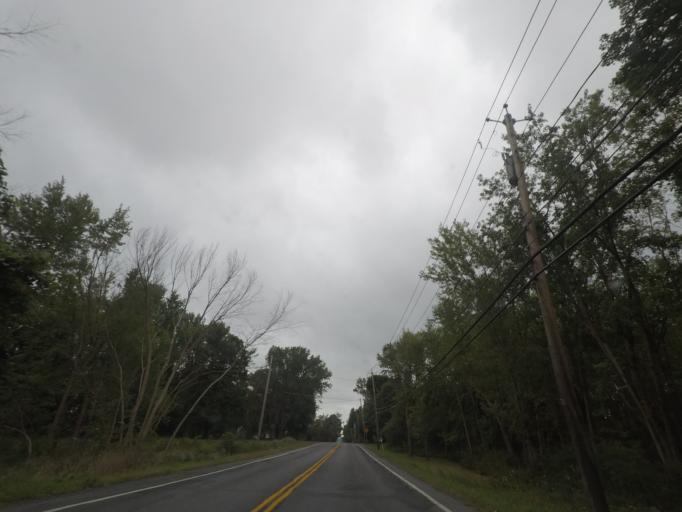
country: US
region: New York
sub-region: Rensselaer County
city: Hoosick Falls
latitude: 42.9226
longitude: -73.3483
